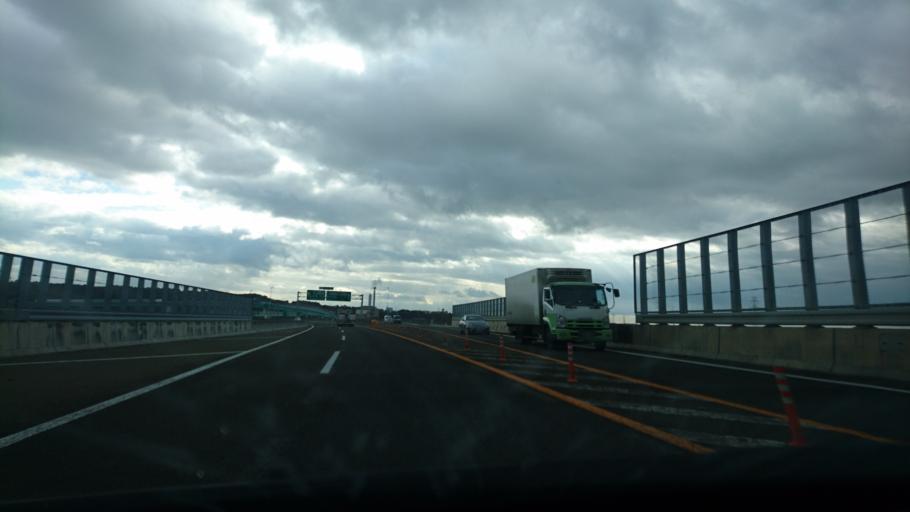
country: JP
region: Miyagi
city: Rifu
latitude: 38.3155
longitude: 140.9707
